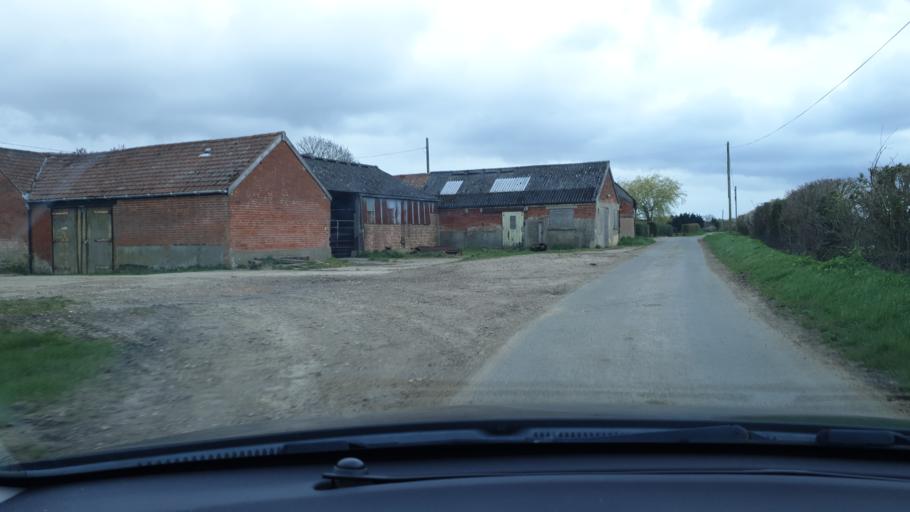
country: GB
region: England
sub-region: Essex
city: Mistley
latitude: 51.8960
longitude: 1.1323
